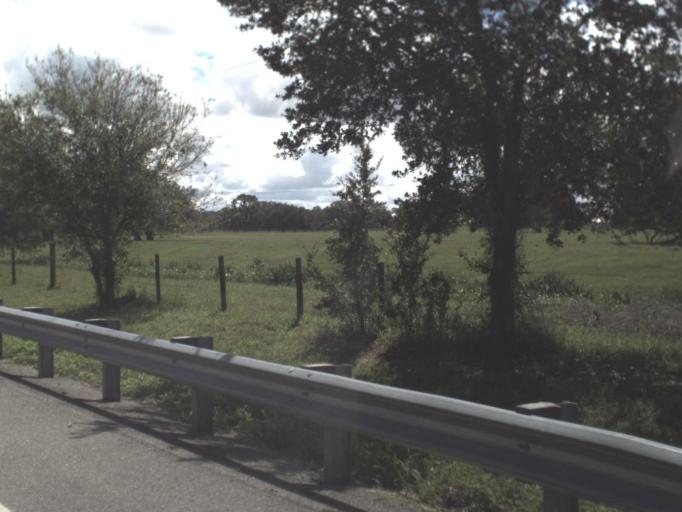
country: US
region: Florida
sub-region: Sarasota County
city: Lake Sarasota
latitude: 27.3792
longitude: -82.2336
